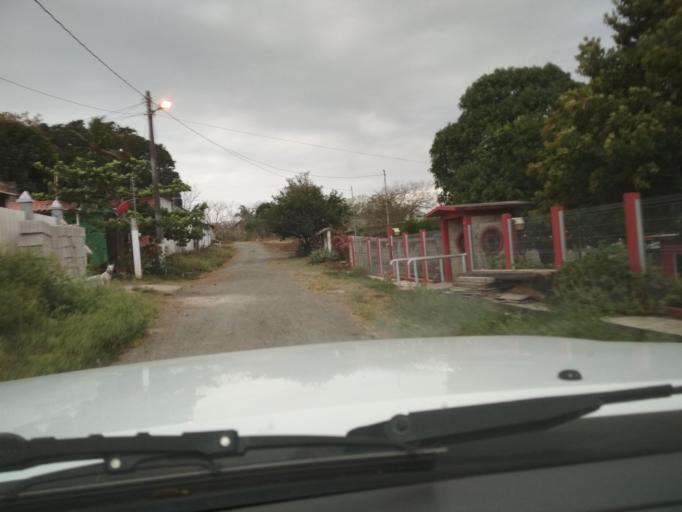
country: MX
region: Veracruz
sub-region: Veracruz
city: Delfino Victoria (Santa Fe)
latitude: 19.1659
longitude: -96.2606
